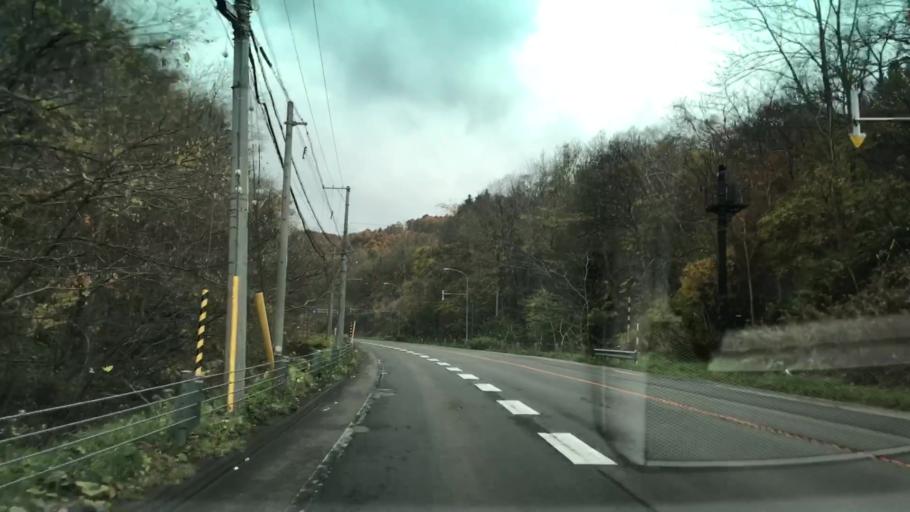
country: JP
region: Hokkaido
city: Yoichi
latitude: 43.2289
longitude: 140.7347
